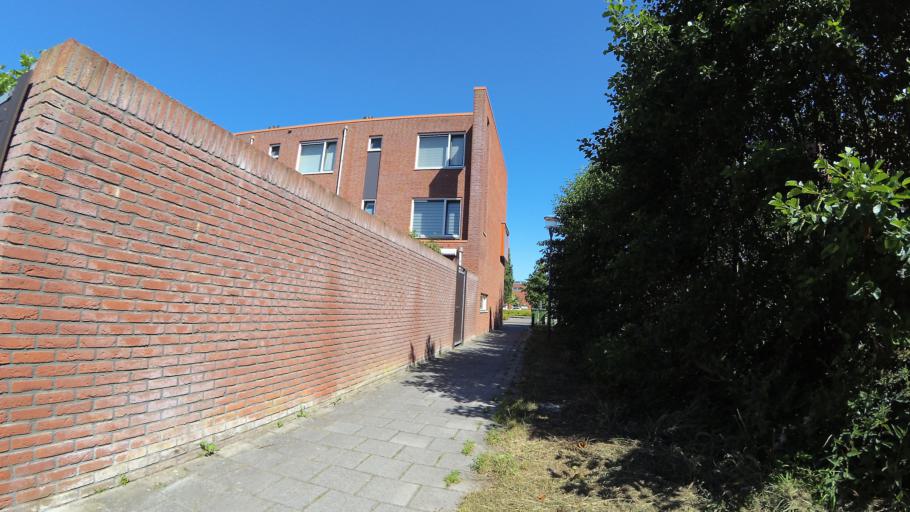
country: NL
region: North Brabant
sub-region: Gemeente Waalwijk
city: Waalwijk
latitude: 51.6742
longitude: 5.0420
